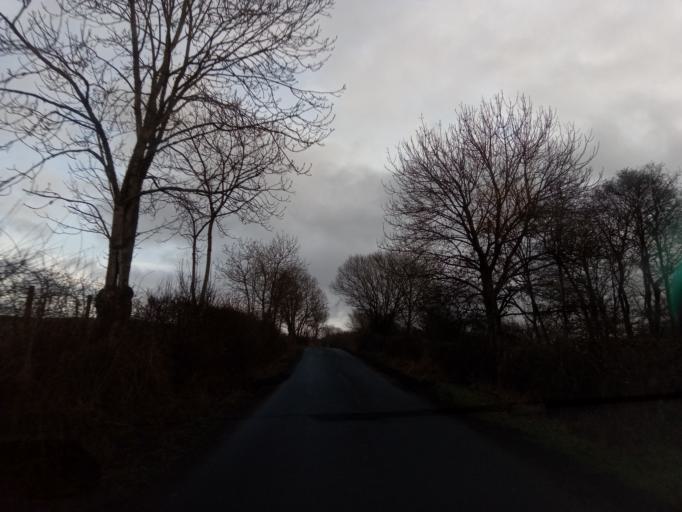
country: GB
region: Scotland
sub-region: The Scottish Borders
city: Selkirk
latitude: 55.5677
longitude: -2.8067
